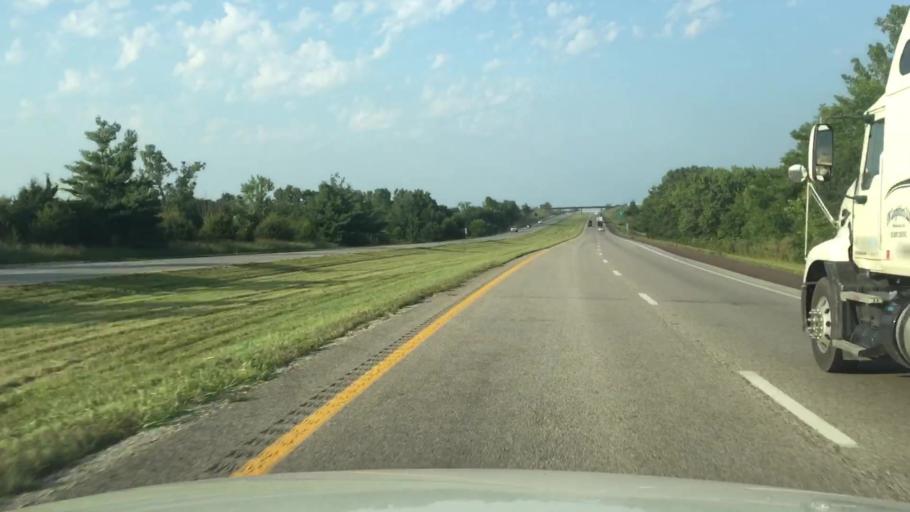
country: US
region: Missouri
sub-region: Daviess County
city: Gallatin
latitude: 39.9250
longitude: -94.1375
